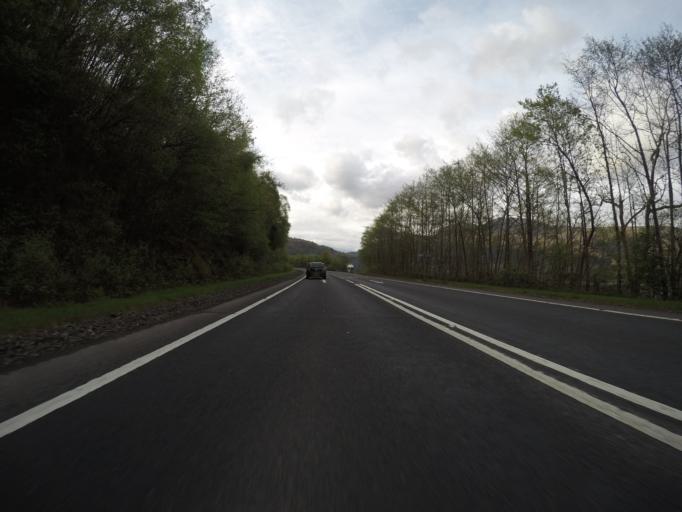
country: GB
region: Scotland
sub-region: Argyll and Bute
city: Helensburgh
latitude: 56.1487
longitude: -4.6651
